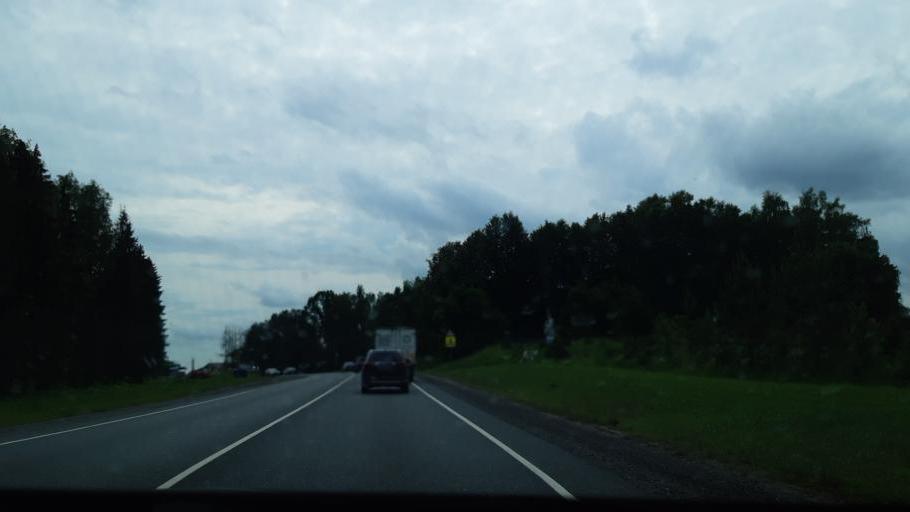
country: RU
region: Moskovskaya
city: Dorokhovo
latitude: 55.5094
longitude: 36.3451
